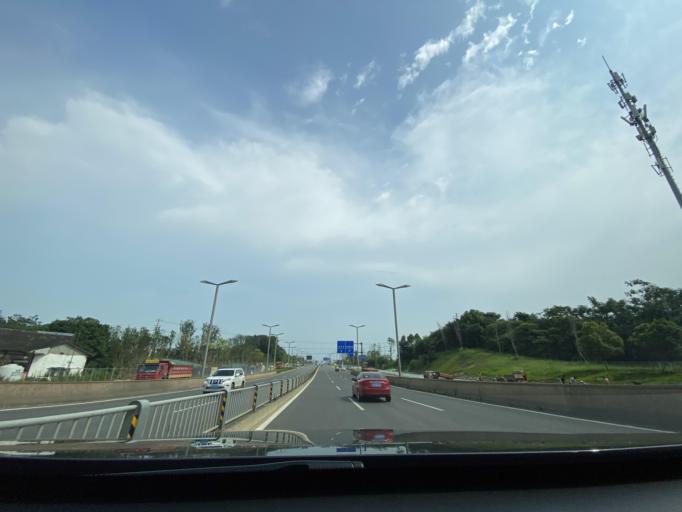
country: CN
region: Sichuan
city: Longquan
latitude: 30.4441
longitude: 104.0950
